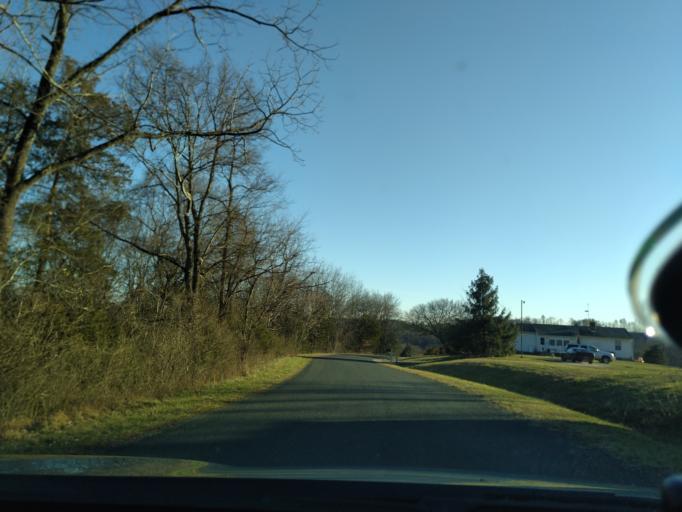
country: US
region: Virginia
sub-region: Appomattox County
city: Appomattox
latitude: 37.3774
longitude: -78.6406
